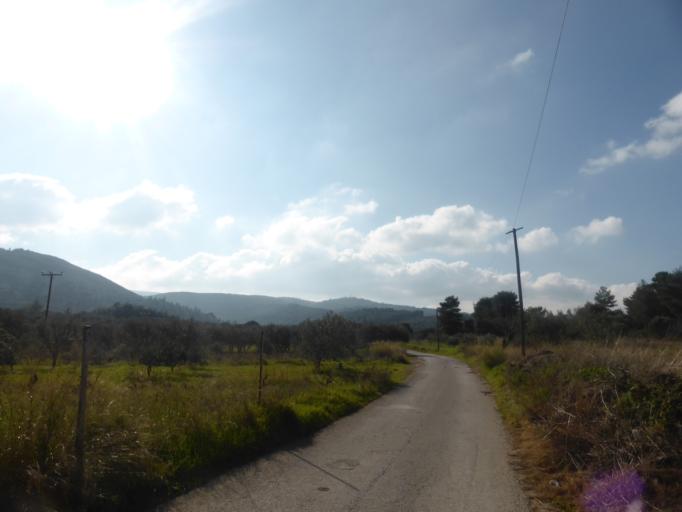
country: GR
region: Attica
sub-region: Nomarchia Anatolikis Attikis
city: Kalamos
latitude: 38.2969
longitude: 23.8474
